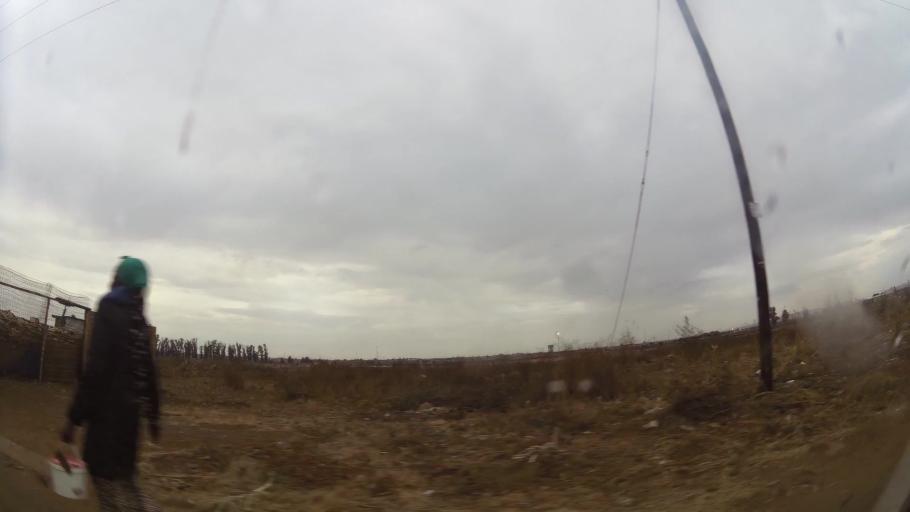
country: ZA
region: Gauteng
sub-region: Ekurhuleni Metropolitan Municipality
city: Germiston
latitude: -26.3717
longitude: 28.1715
